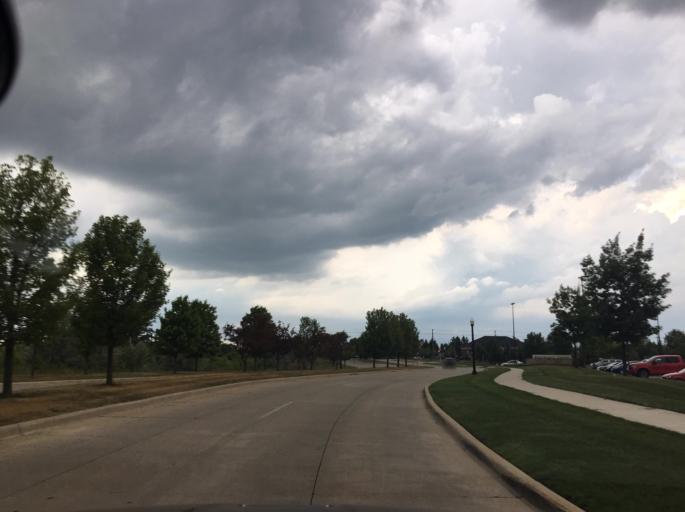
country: US
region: Michigan
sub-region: Macomb County
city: Clinton
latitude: 42.6252
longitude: -82.9502
